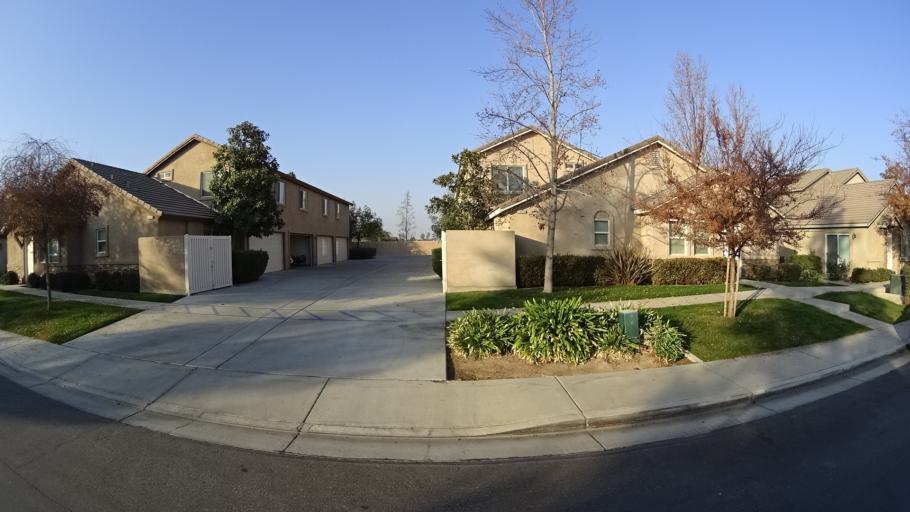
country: US
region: California
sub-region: Kern County
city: Rosedale
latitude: 35.3828
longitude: -119.1498
